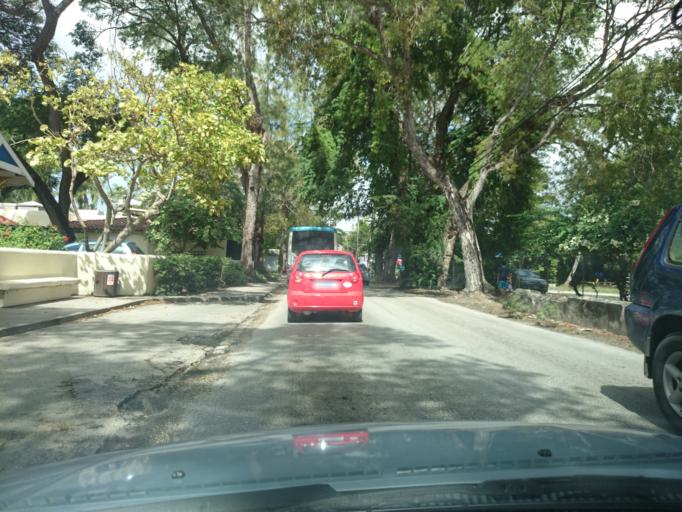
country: BB
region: Saint James
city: Holetown
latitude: 13.1632
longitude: -59.6369
